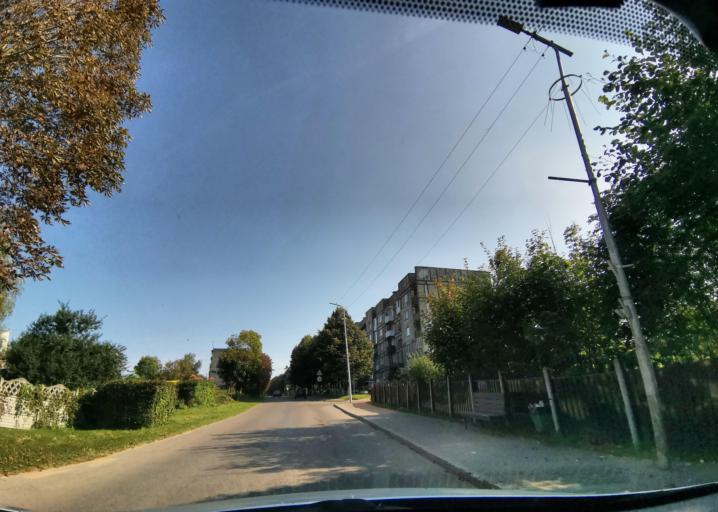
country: RU
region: Kaliningrad
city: Neman
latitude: 55.0354
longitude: 22.0333
